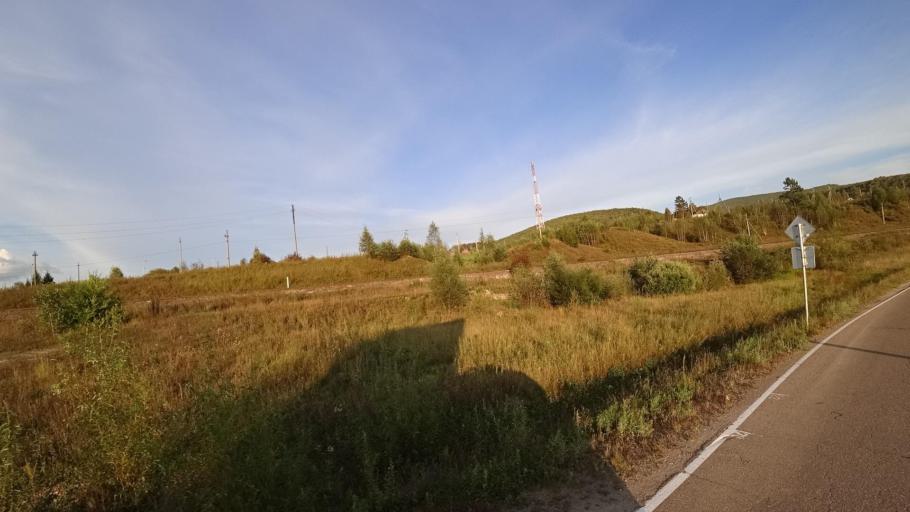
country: RU
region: Jewish Autonomous Oblast
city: Kul'dur
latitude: 49.2034
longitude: 131.6369
